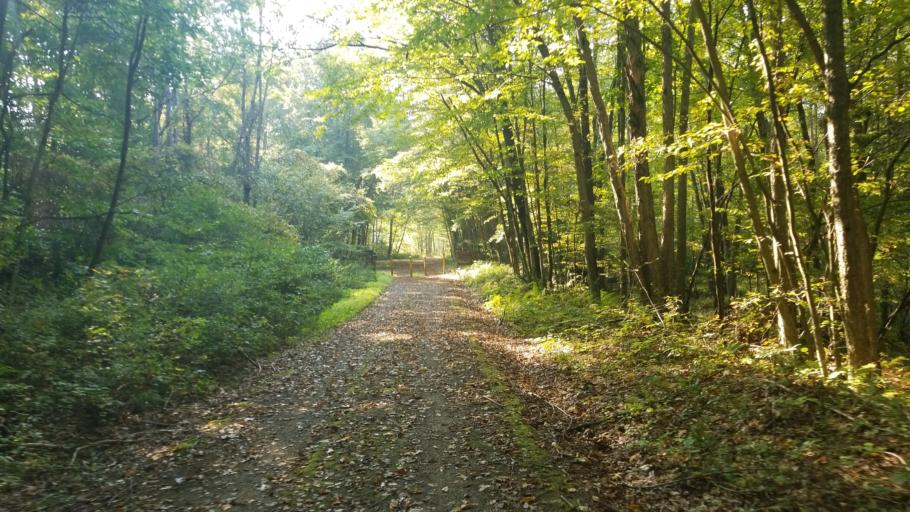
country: US
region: Pennsylvania
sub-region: Jefferson County
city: Brockway
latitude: 41.3570
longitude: -78.8190
